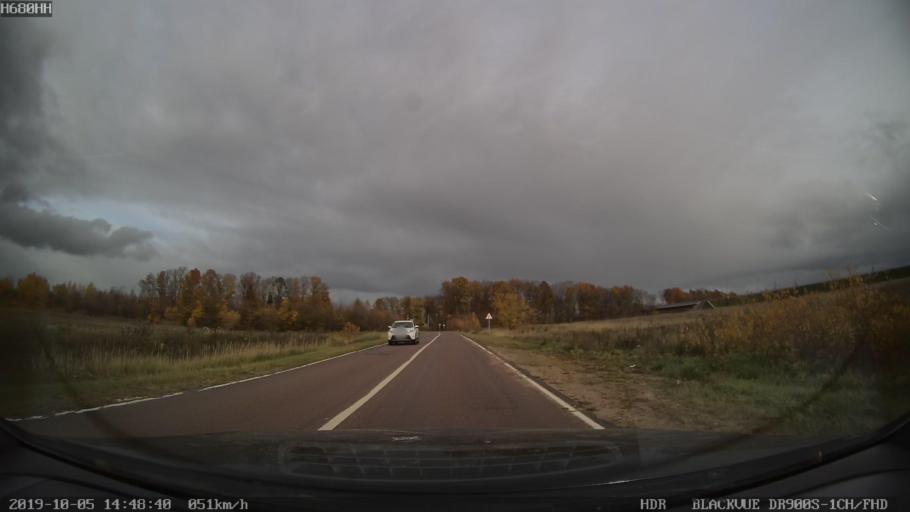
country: RU
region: Moskovskaya
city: Solnechnogorsk
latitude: 56.2163
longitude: 36.8997
